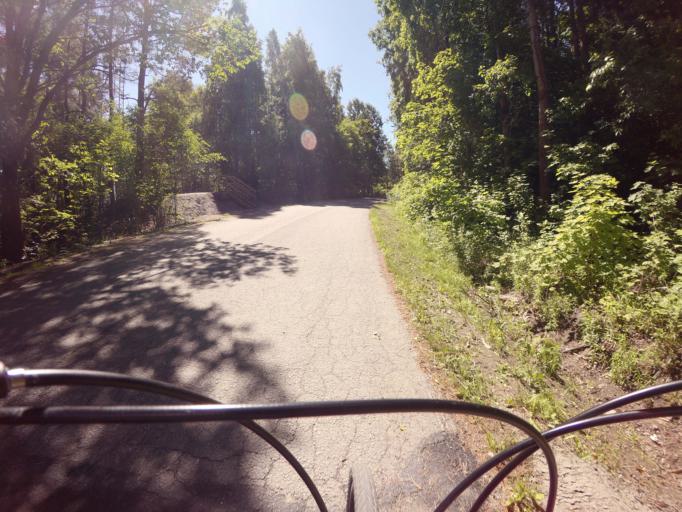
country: FI
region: Varsinais-Suomi
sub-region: Turku
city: Raisio
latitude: 60.4530
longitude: 22.2112
